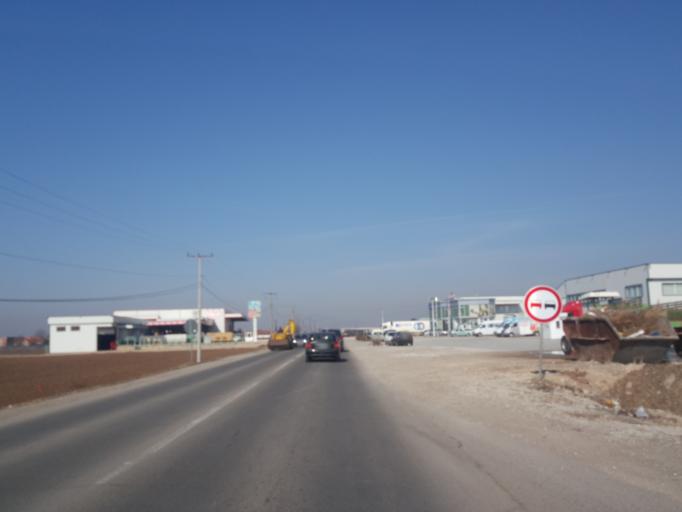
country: XK
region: Mitrovica
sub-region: Vushtrri
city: Vushtrri
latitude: 42.7832
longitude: 21.0111
